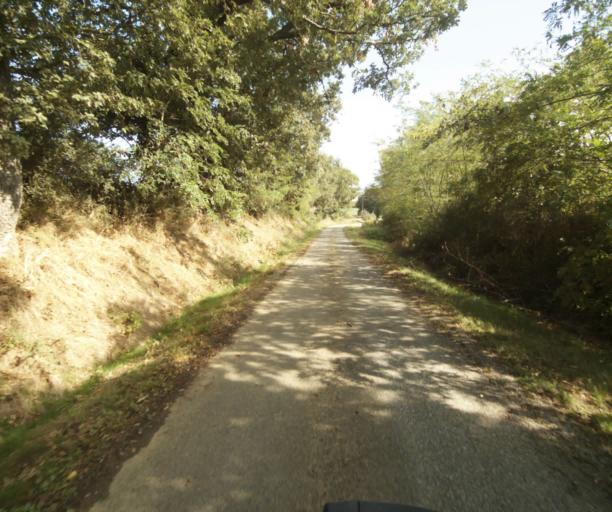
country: FR
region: Midi-Pyrenees
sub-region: Departement du Tarn-et-Garonne
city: Verdun-sur-Garonne
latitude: 43.8470
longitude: 1.1949
